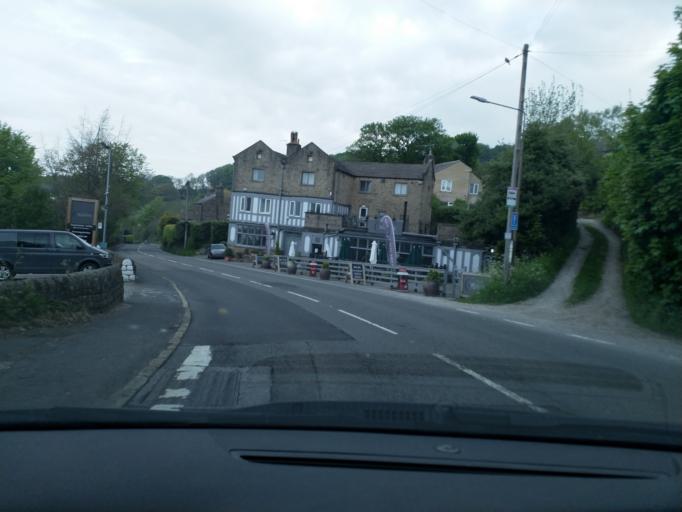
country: GB
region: England
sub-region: Derbyshire
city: Hathersage
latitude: 53.3232
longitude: -1.6395
